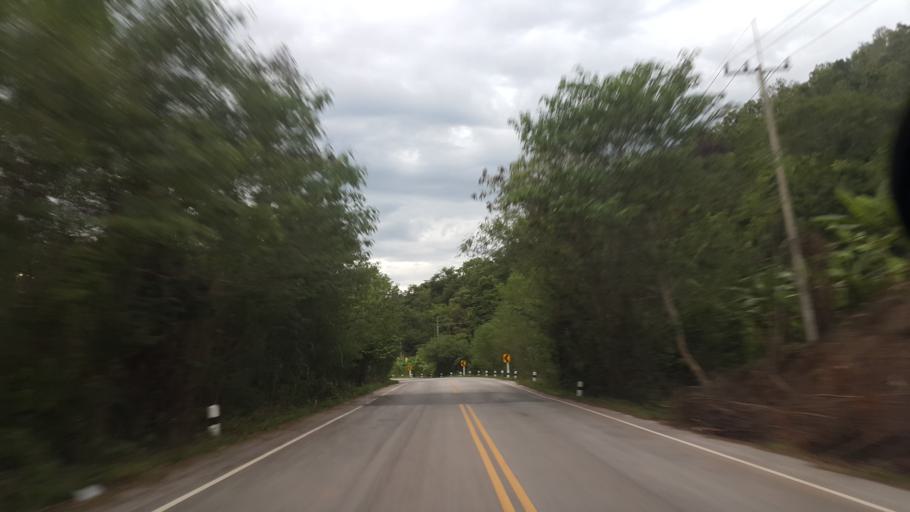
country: TH
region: Loei
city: Na Haeo
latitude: 17.5019
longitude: 101.1842
